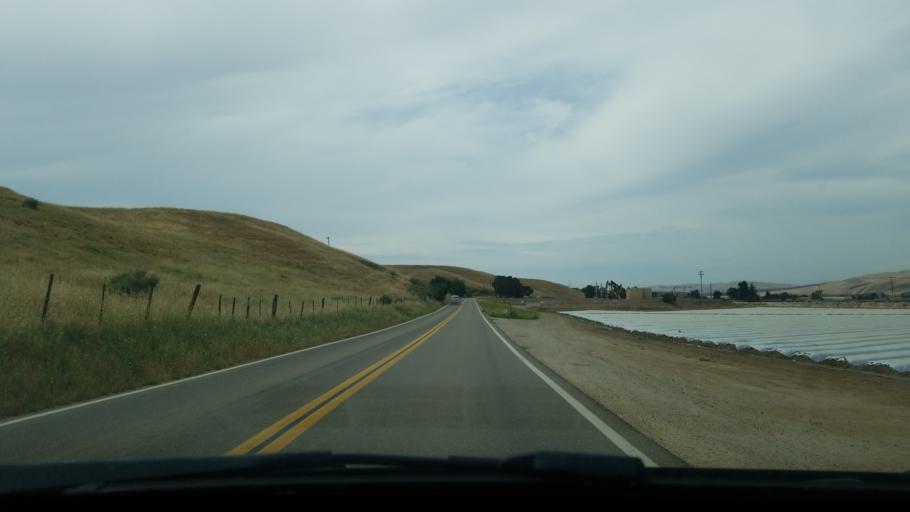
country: US
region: California
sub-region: Santa Barbara County
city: Orcutt
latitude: 34.8737
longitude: -120.3078
